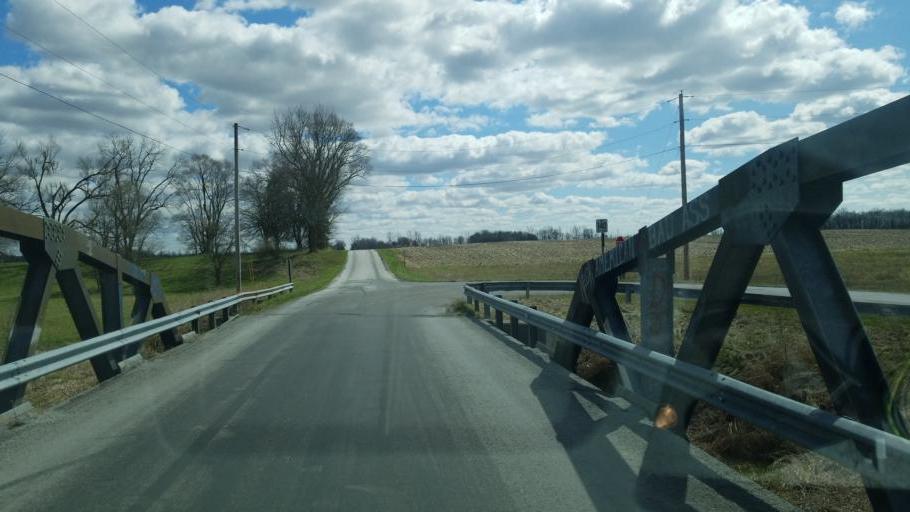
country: US
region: Ohio
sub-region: Hardin County
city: Kenton
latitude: 40.6333
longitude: -83.5617
